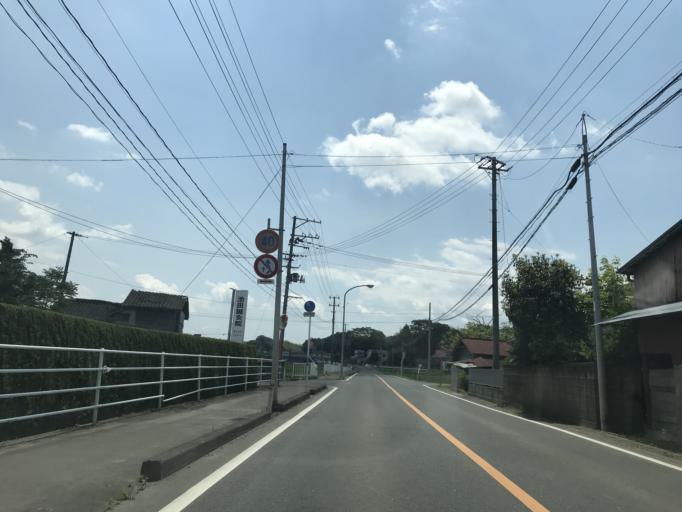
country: JP
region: Miyagi
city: Kogota
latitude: 38.5084
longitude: 141.0693
